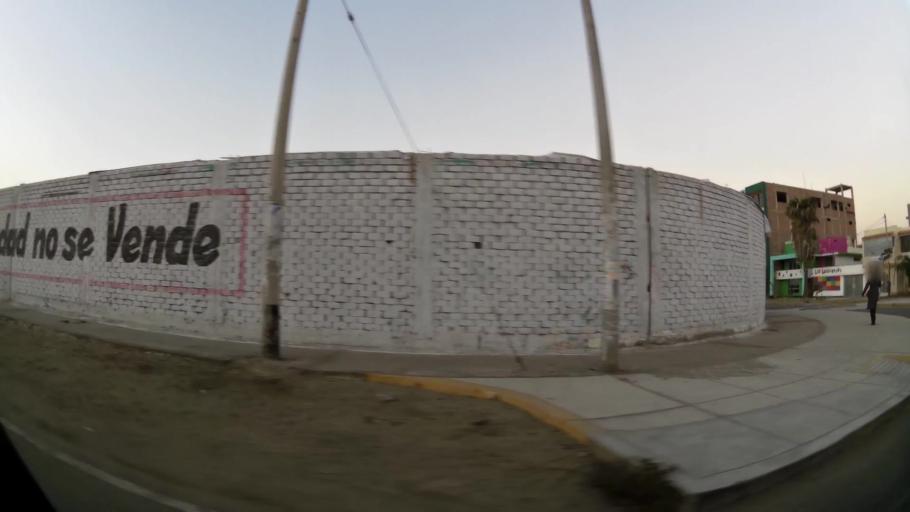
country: PE
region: Ancash
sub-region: Provincia de Santa
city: Buenos Aires
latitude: -9.1255
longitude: -78.5338
